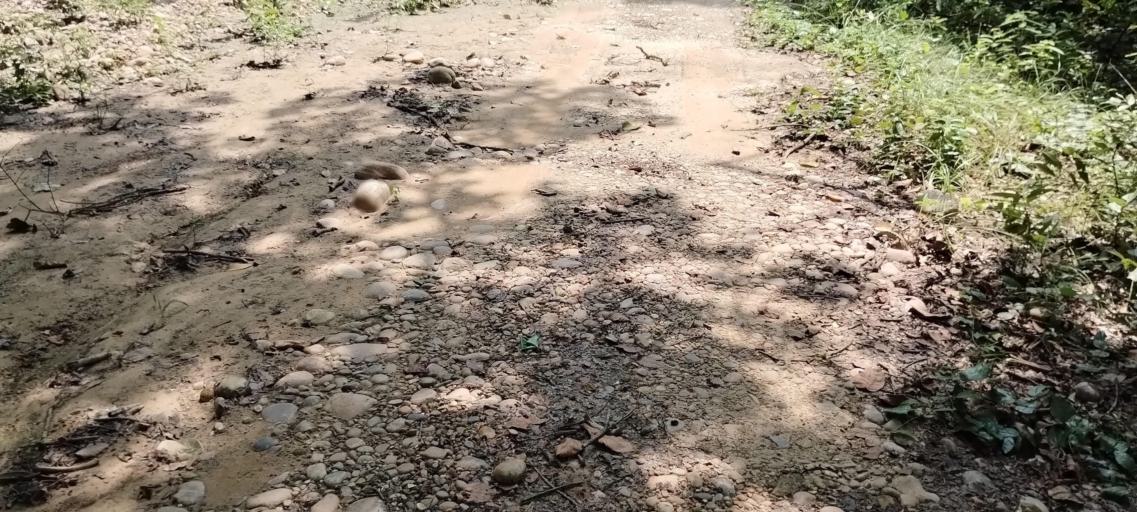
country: NP
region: Far Western
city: Tikapur
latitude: 28.4980
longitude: 81.2561
